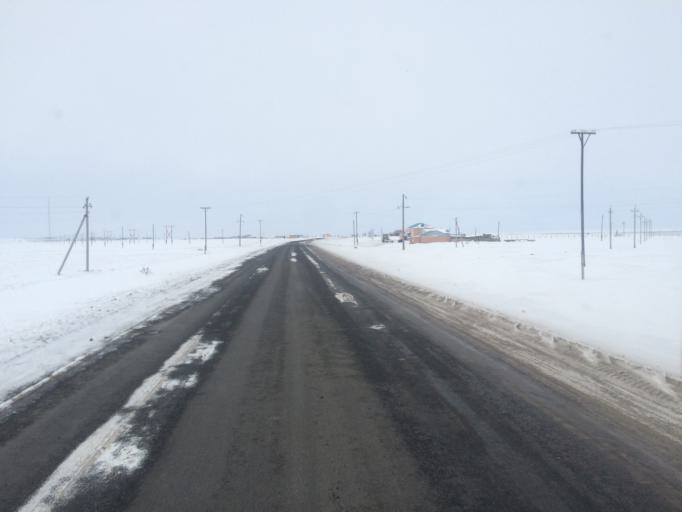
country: RU
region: Orenburg
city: Dombarovskiy
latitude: 49.9579
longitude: 60.0828
